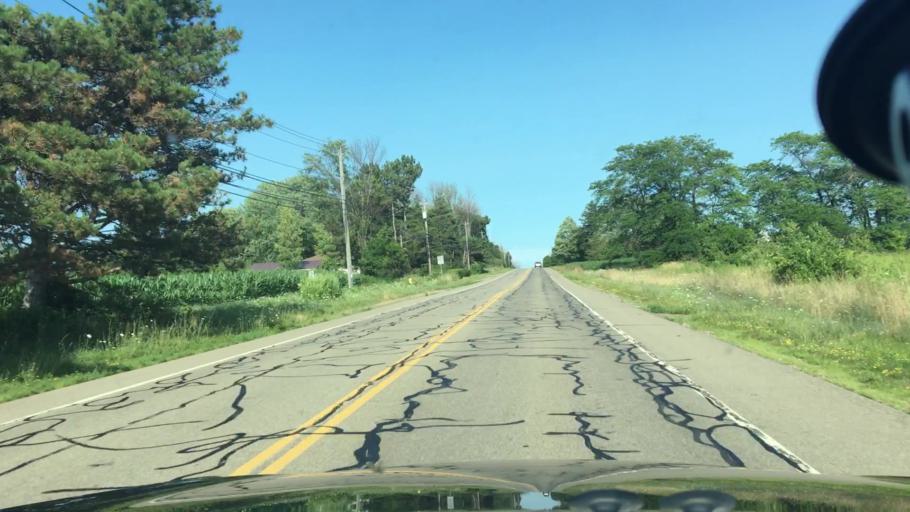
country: US
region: New York
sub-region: Erie County
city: Angola
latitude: 42.6525
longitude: -79.0038
